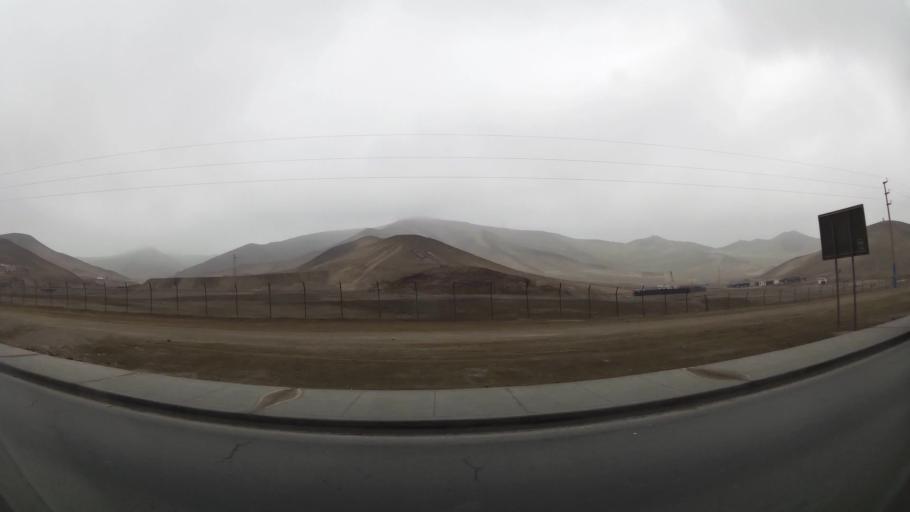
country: PE
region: Lima
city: Ventanilla
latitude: -11.9055
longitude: -77.1285
